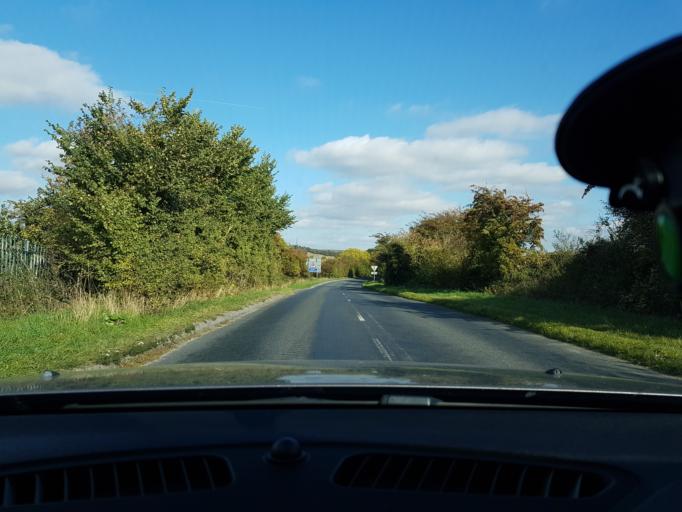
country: GB
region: England
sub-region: Borough of Swindon
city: Wanborough
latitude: 51.5242
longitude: -1.6877
